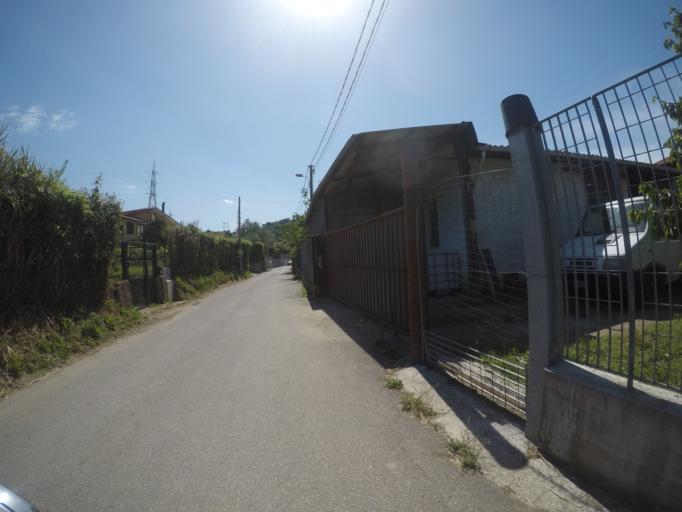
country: IT
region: Tuscany
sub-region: Provincia di Massa-Carrara
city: Carrara
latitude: 44.0425
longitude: 10.0907
